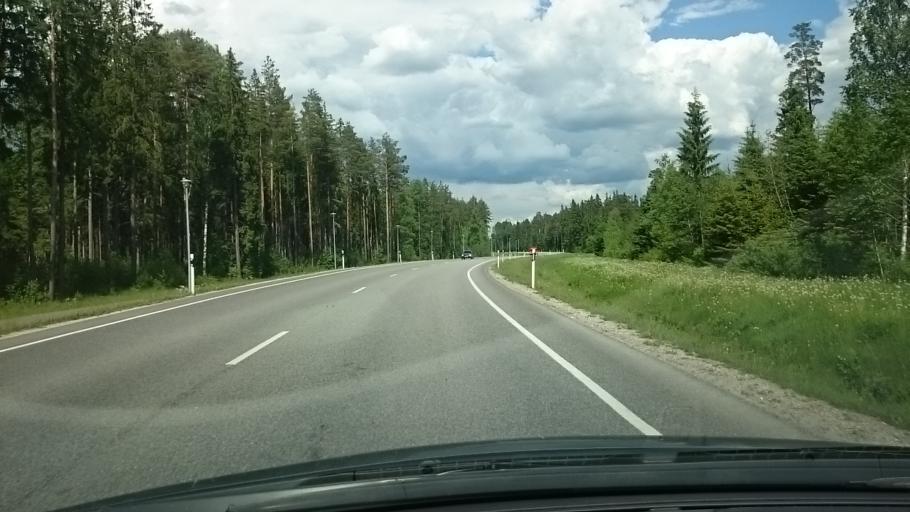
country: EE
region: Jaervamaa
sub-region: Paide linn
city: Paide
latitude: 58.8601
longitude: 25.4883
